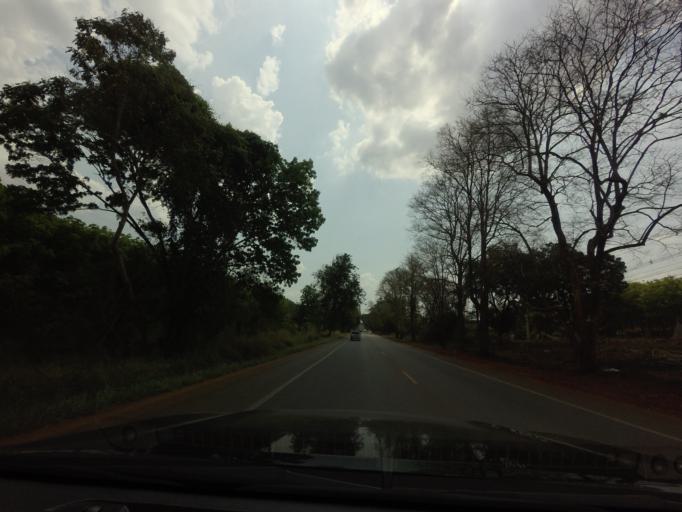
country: TH
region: Kanchanaburi
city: Sai Yok
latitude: 14.1613
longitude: 99.1367
